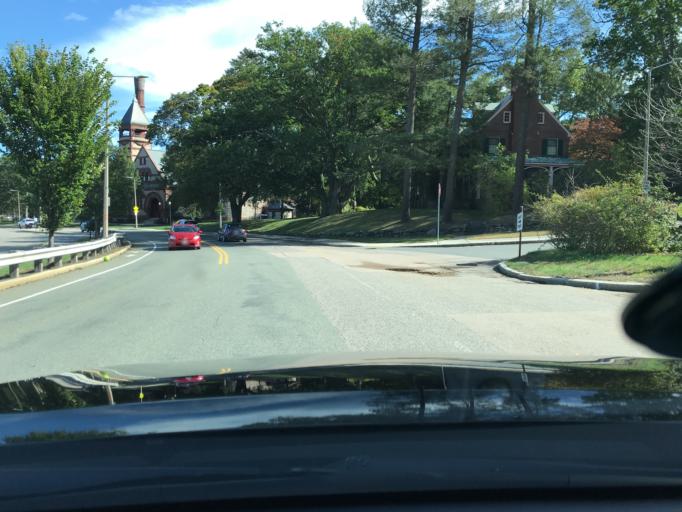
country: US
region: Massachusetts
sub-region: Norfolk County
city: Brookline
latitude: 42.3316
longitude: -71.1578
